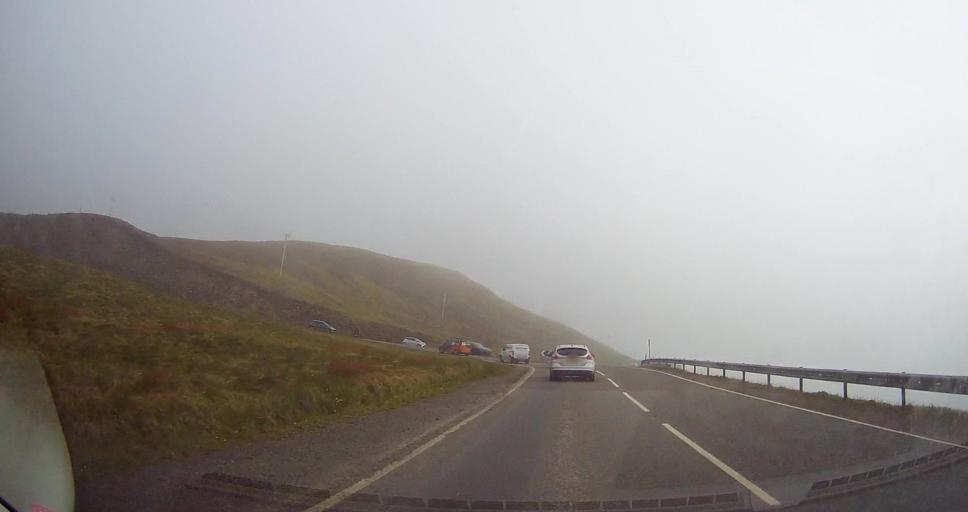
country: GB
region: Scotland
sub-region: Shetland Islands
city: Lerwick
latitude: 60.1400
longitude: -1.2609
